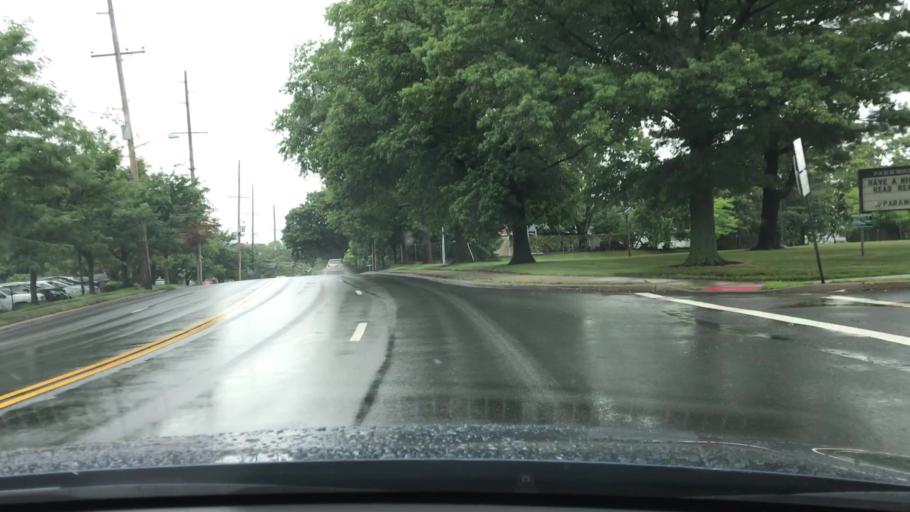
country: US
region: New Jersey
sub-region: Bergen County
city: Paramus
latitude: 40.9657
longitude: -74.0686
